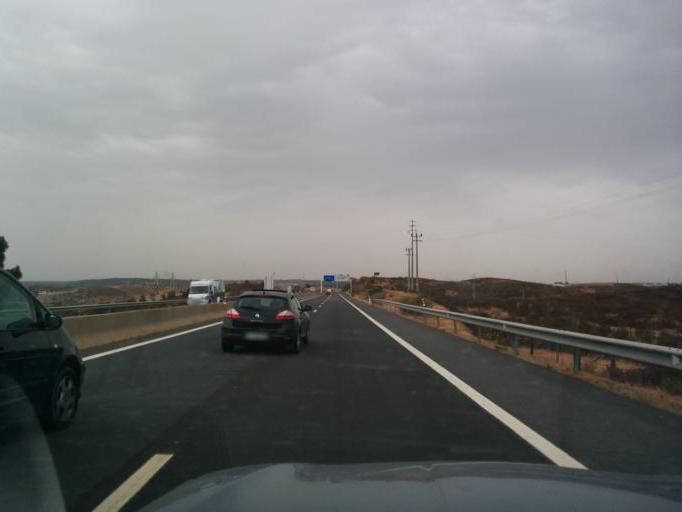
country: PT
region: Faro
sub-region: Castro Marim
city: Castro Marim
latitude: 37.2295
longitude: -7.4580
